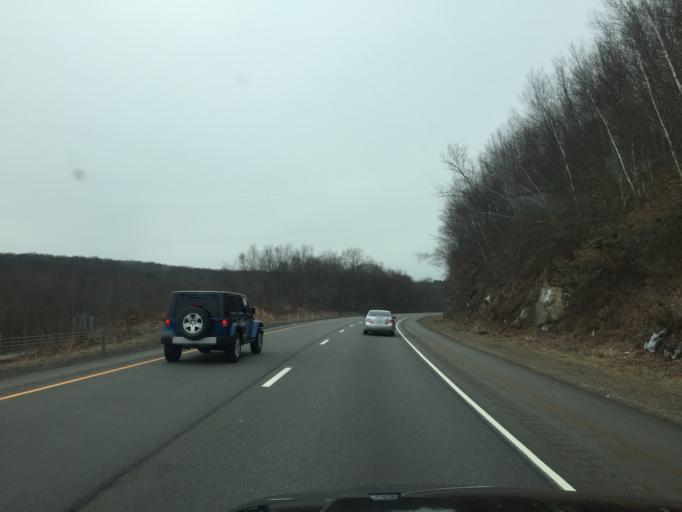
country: US
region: Connecticut
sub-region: Hartford County
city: Terramuggus
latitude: 41.6277
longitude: -72.4459
